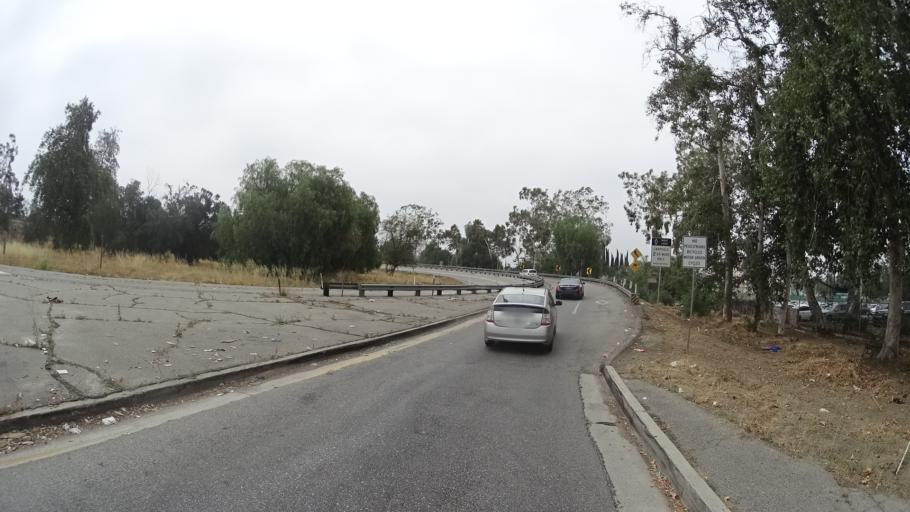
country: US
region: California
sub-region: Los Angeles County
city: North Hollywood
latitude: 34.1864
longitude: -118.4030
